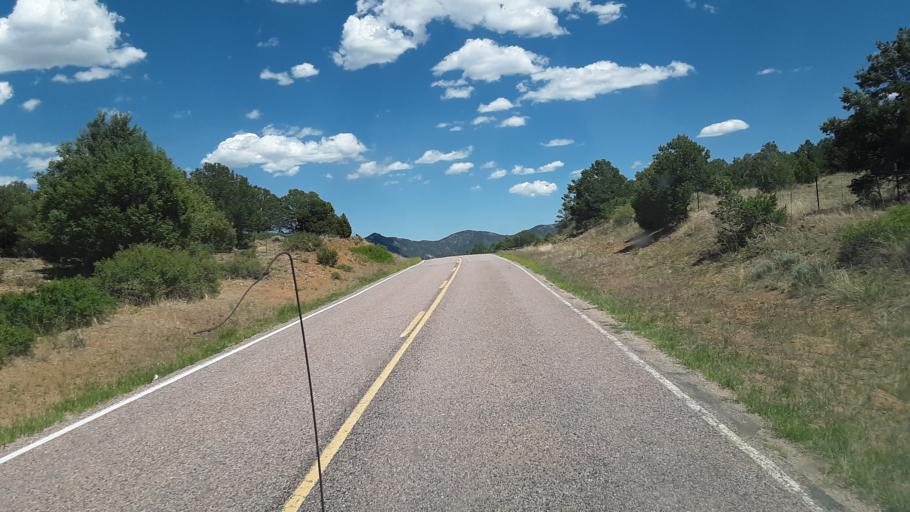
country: US
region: Colorado
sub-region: Custer County
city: Westcliffe
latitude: 38.3092
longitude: -105.6401
